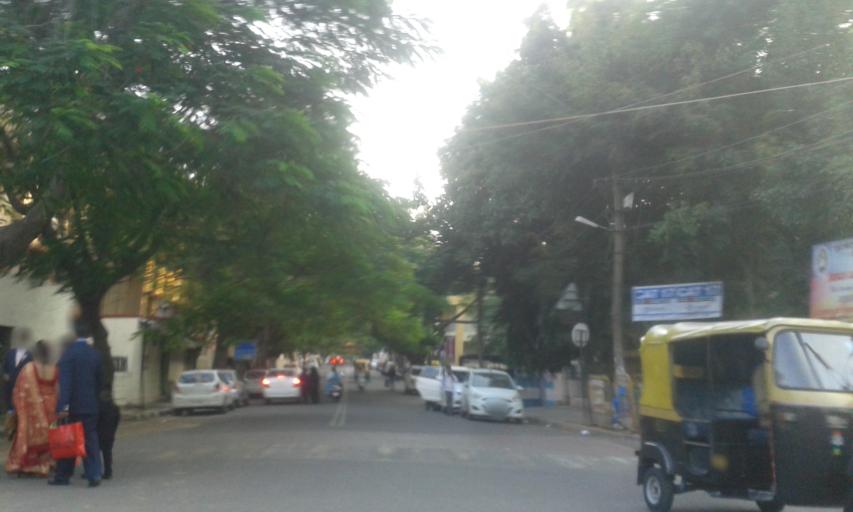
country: IN
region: Karnataka
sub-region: Bangalore Urban
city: Bangalore
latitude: 12.9278
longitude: 77.5882
